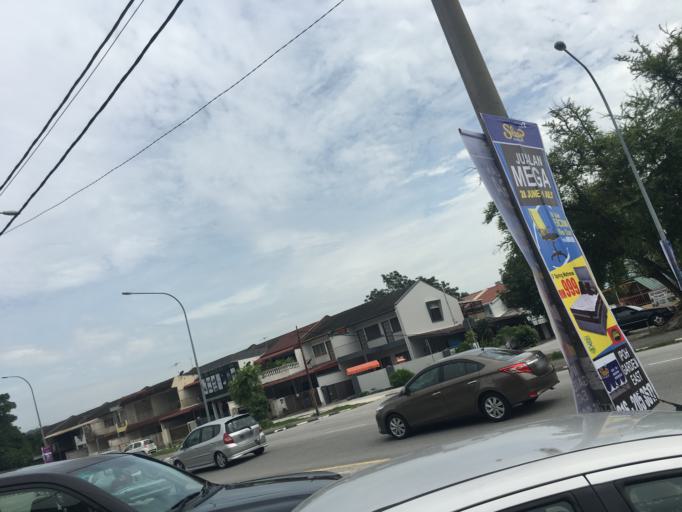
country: MY
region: Perak
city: Ipoh
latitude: 4.6120
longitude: 101.1076
